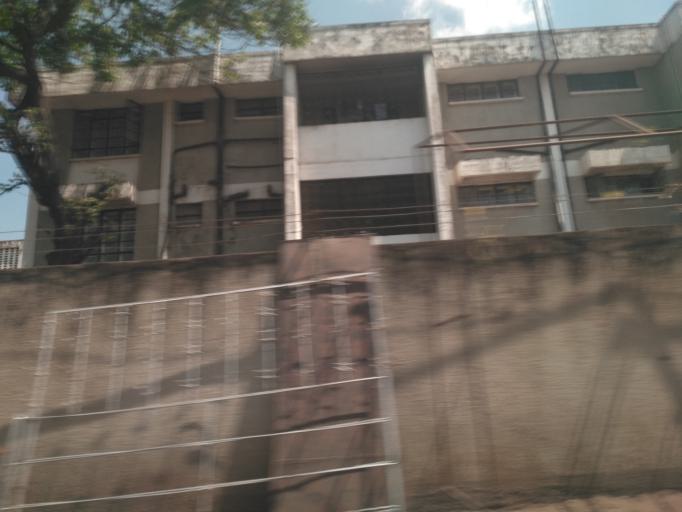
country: TZ
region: Arusha
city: Arusha
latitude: -3.3685
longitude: 36.6834
